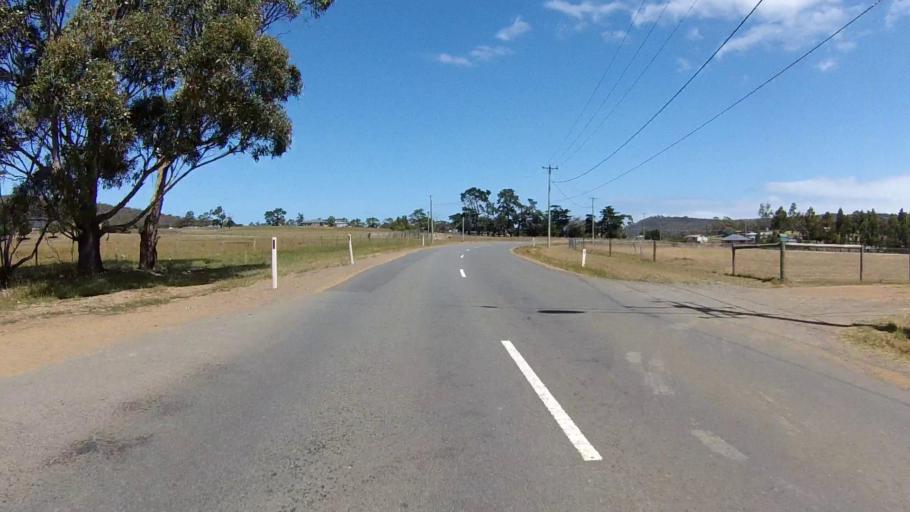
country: AU
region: Tasmania
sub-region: Clarence
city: Sandford
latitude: -42.9516
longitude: 147.4808
